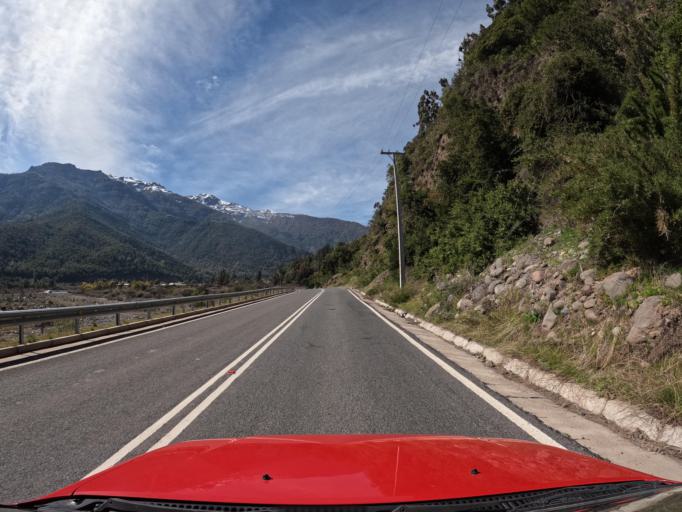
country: CL
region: Maule
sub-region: Provincia de Curico
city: Teno
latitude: -35.0028
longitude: -70.8255
